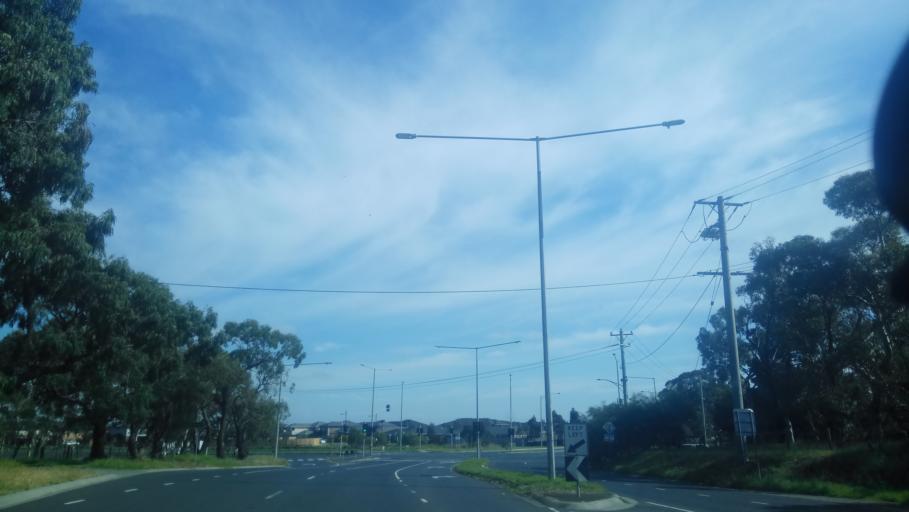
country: AU
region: Victoria
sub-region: Greater Dandenong
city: Keysborough
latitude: -38.0125
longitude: 145.1726
